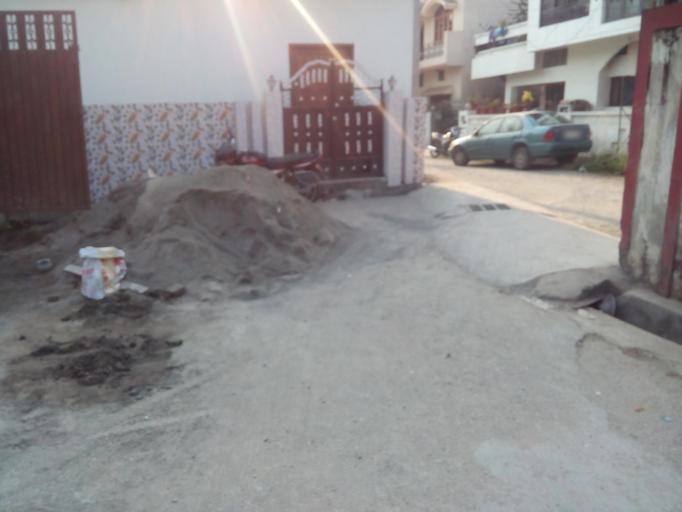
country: IN
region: Uttarakhand
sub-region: Dehradun
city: Dehradun
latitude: 30.3075
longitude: 78.0127
